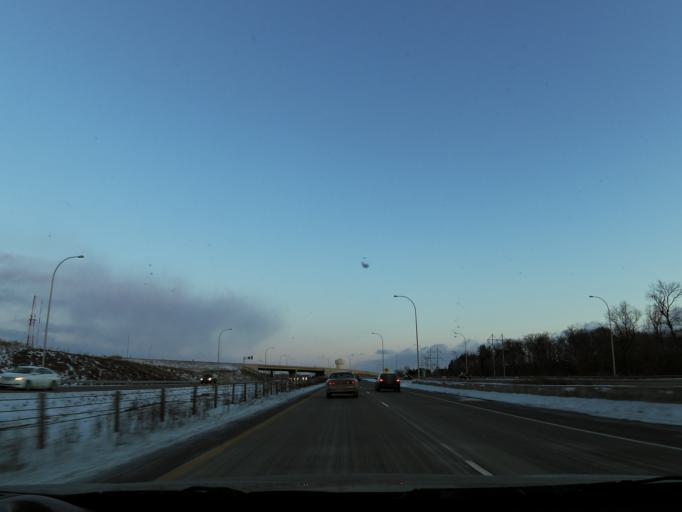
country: US
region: Minnesota
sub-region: Ramsey County
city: Arden Hills
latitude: 45.0645
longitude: -93.1628
